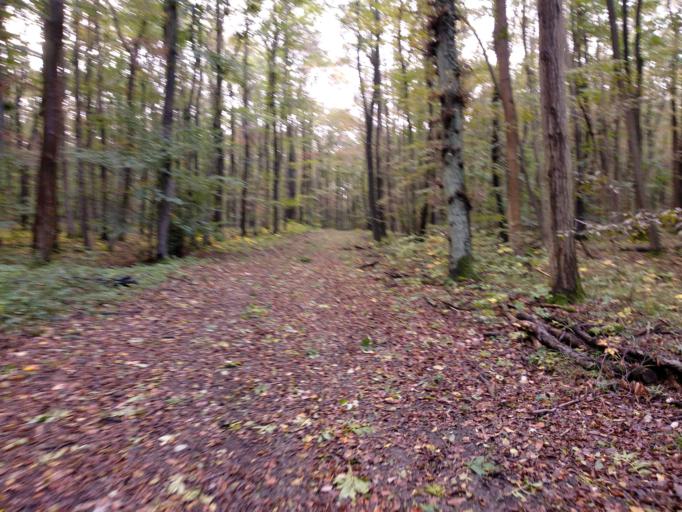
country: DE
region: North Rhine-Westphalia
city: Beverungen
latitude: 51.6467
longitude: 9.3641
